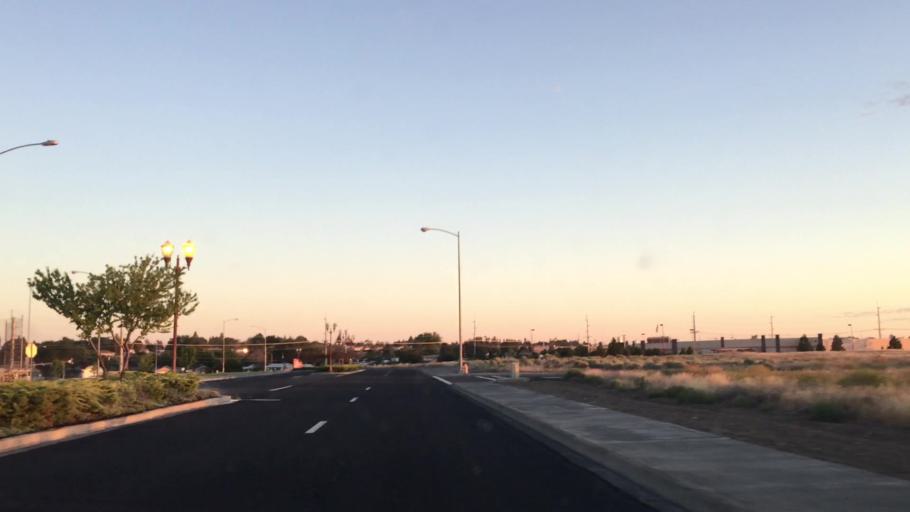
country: US
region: Washington
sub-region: Grant County
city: Moses Lake
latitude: 47.1446
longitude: -119.2899
